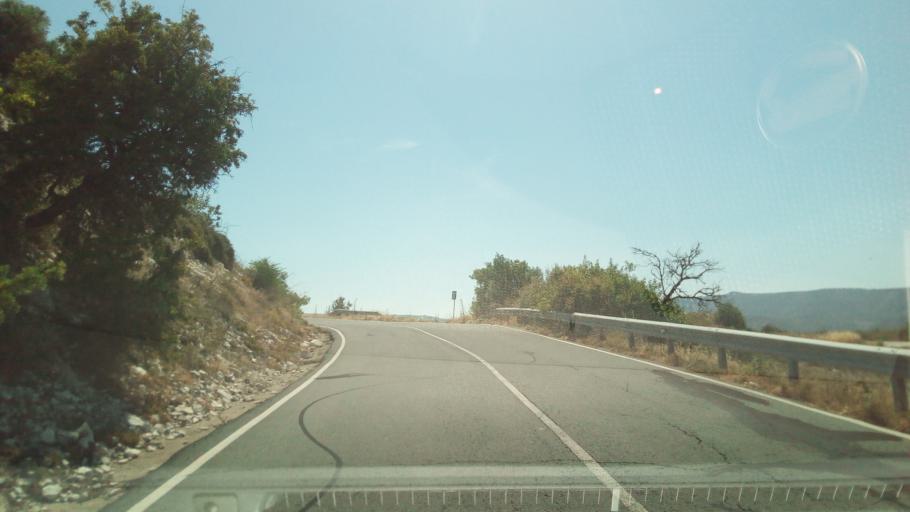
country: CY
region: Limassol
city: Pachna
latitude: 34.7980
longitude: 32.6885
